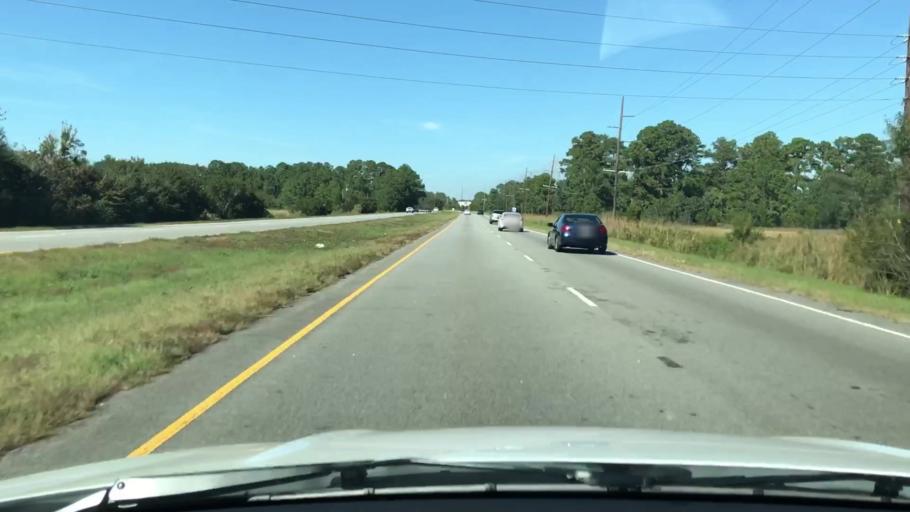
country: US
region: South Carolina
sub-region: Beaufort County
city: Laurel Bay
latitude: 32.5004
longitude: -80.7438
